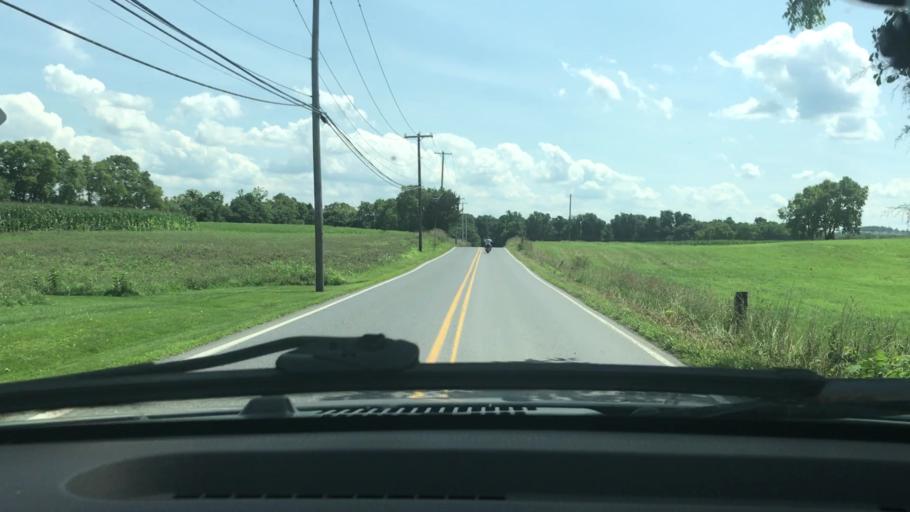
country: US
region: Pennsylvania
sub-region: Dauphin County
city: Hummelstown
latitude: 40.2459
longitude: -76.7356
